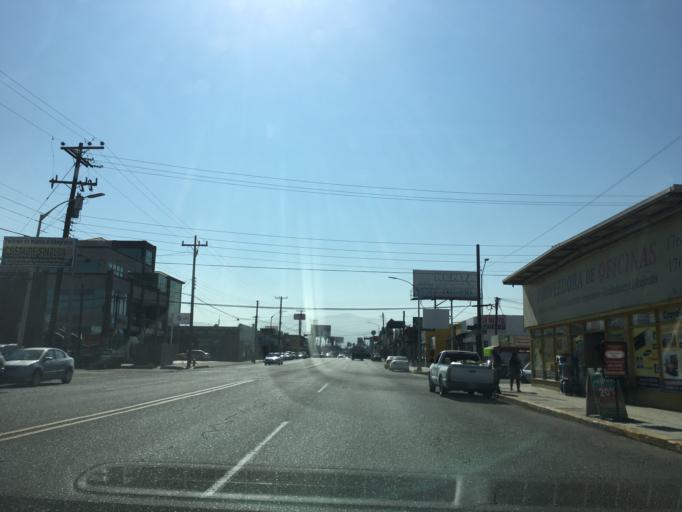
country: MX
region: Baja California
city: Ensenada
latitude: 31.8624
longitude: -116.6116
